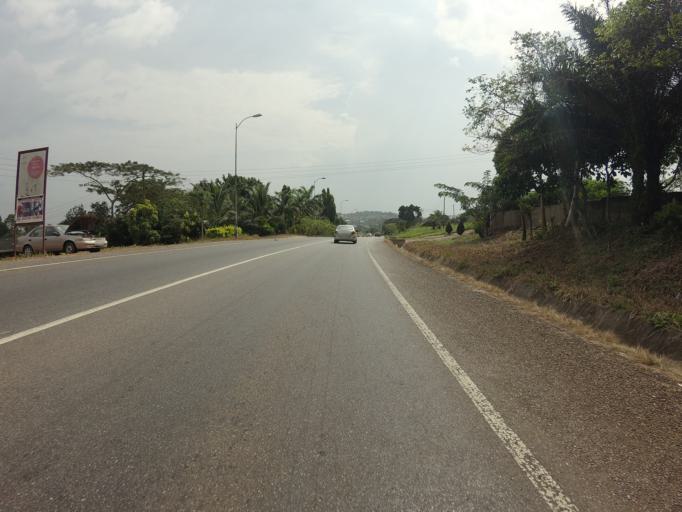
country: GH
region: Eastern
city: Aburi
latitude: 5.8270
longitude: -0.1851
